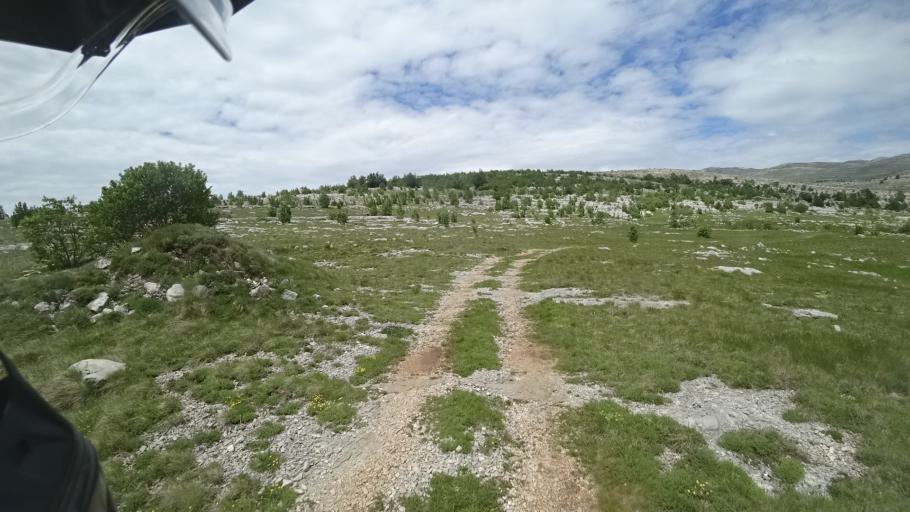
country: HR
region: Splitsko-Dalmatinska
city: Hrvace
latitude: 43.8922
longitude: 16.5851
